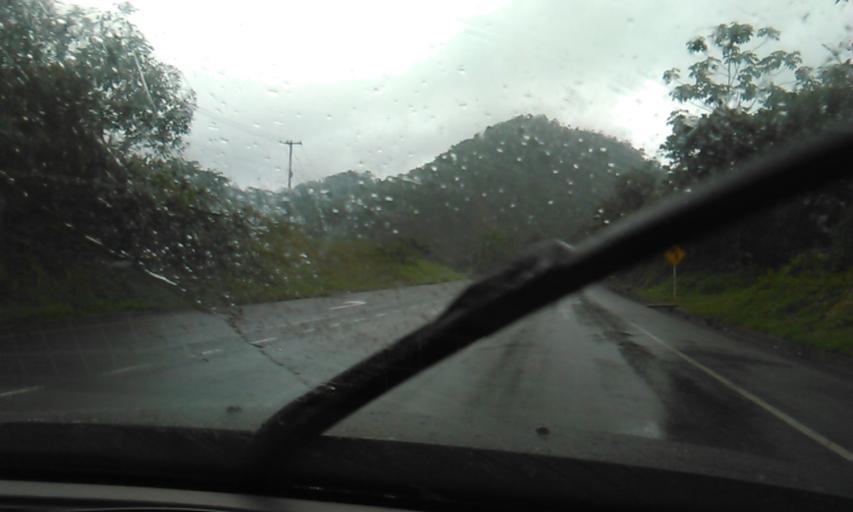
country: CO
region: Valle del Cauca
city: Buenaventura
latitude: 3.8630
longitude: -76.8304
